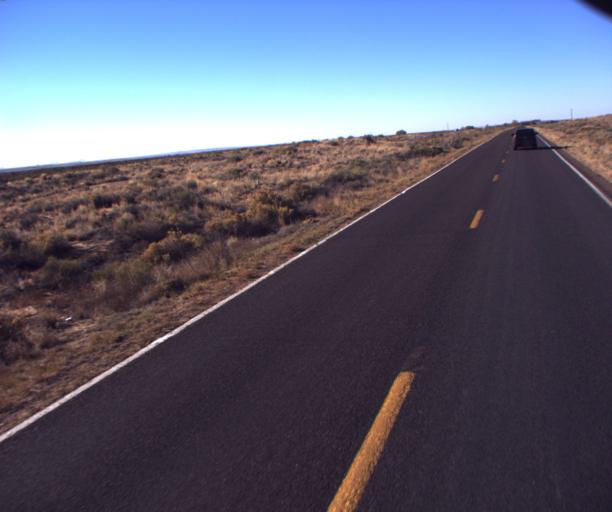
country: US
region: Arizona
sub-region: Navajo County
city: First Mesa
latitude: 35.8107
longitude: -110.4123
